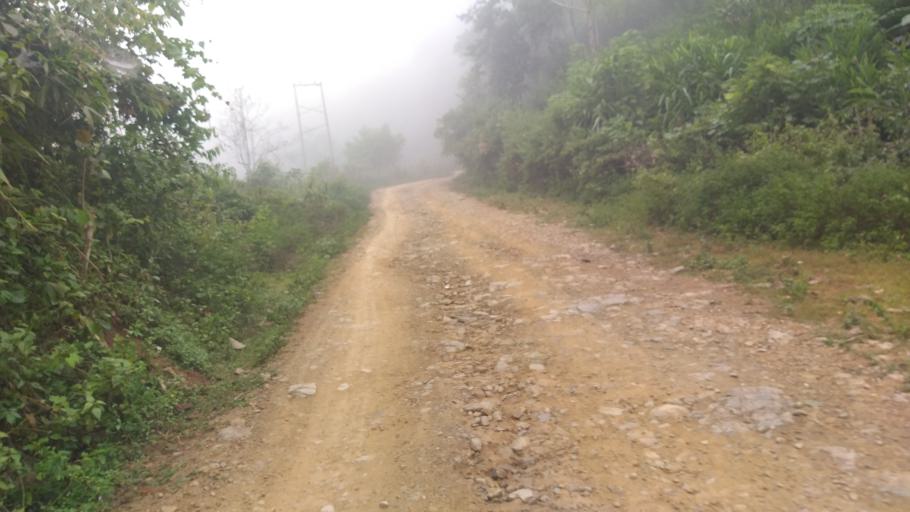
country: LA
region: Phongsali
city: Khoa
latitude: 21.2577
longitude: 102.6661
